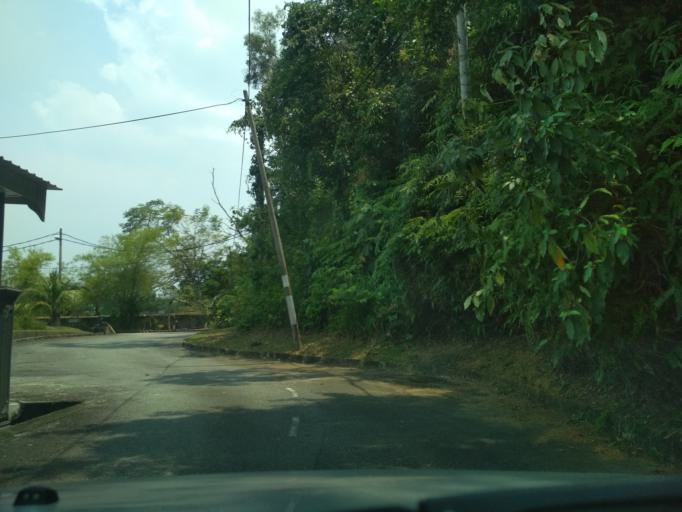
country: MY
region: Kedah
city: Kulim
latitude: 5.3604
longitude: 100.5355
